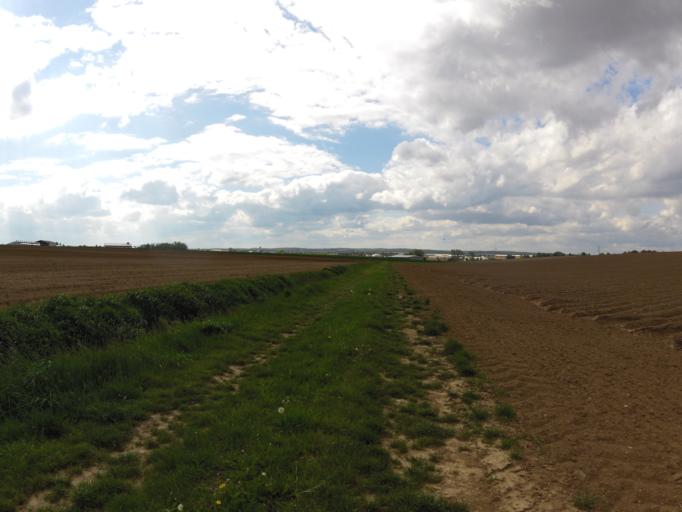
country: DE
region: Bavaria
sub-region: Regierungsbezirk Unterfranken
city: Oberpleichfeld
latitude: 49.8655
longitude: 10.0686
